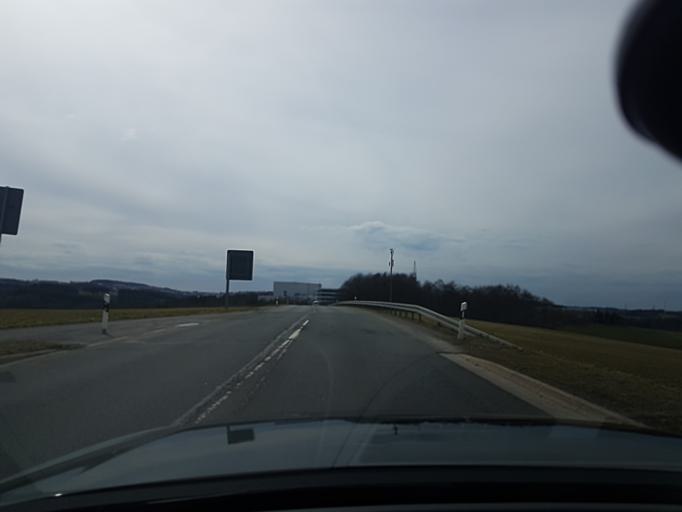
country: DE
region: North Rhine-Westphalia
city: Altena
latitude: 51.2401
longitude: 7.6876
